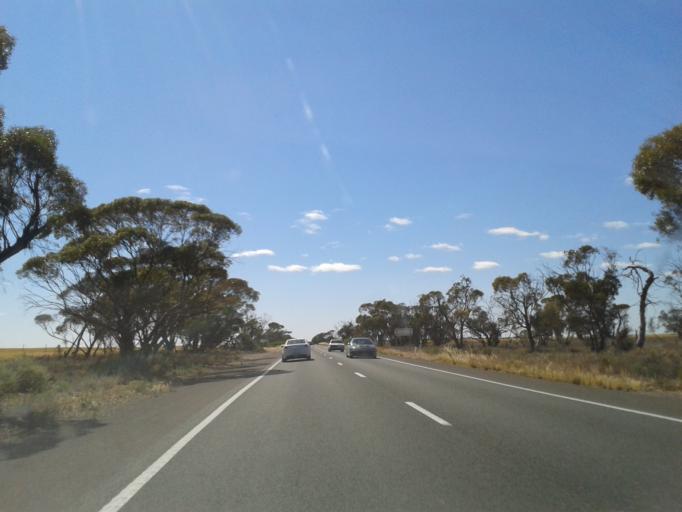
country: AU
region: New South Wales
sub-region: Wentworth
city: Dareton
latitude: -34.2549
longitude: 141.8929
